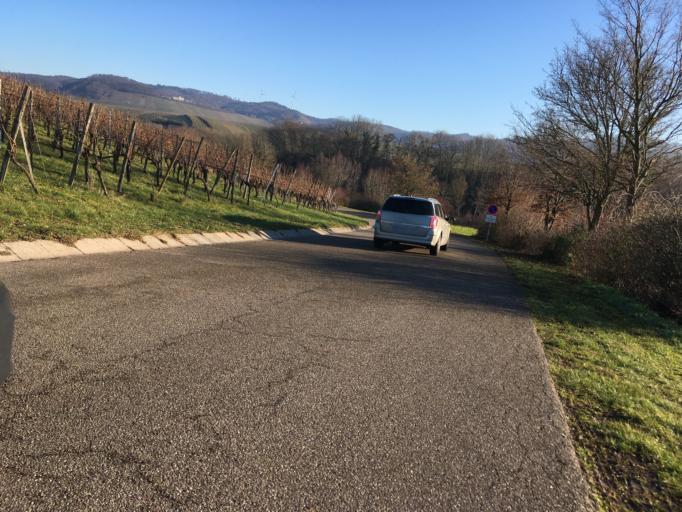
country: DE
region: Baden-Wuerttemberg
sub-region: Regierungsbezirk Stuttgart
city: Lowenstein
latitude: 49.1144
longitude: 9.3782
